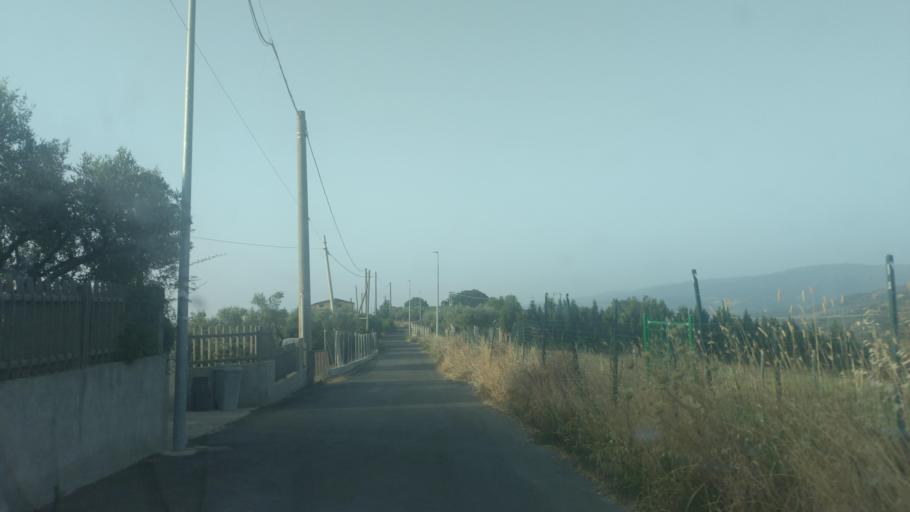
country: IT
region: Calabria
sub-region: Provincia di Catanzaro
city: Staletti
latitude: 38.7626
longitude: 16.5330
